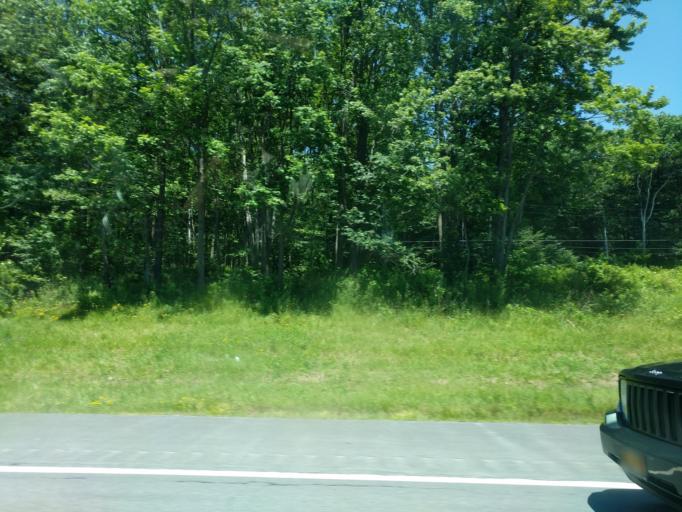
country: US
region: New York
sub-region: Sullivan County
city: Monticello
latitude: 41.6700
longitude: -74.7092
